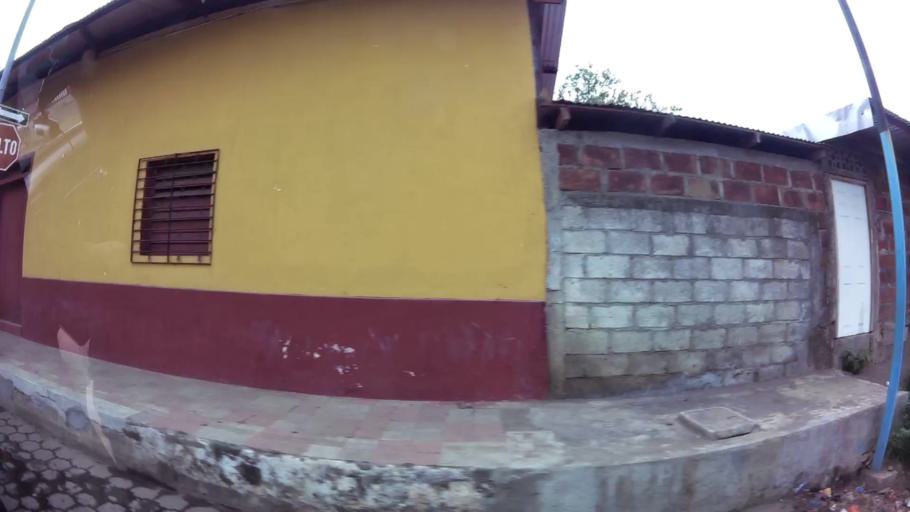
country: NI
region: Leon
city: Leon
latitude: 12.4294
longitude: -86.8743
